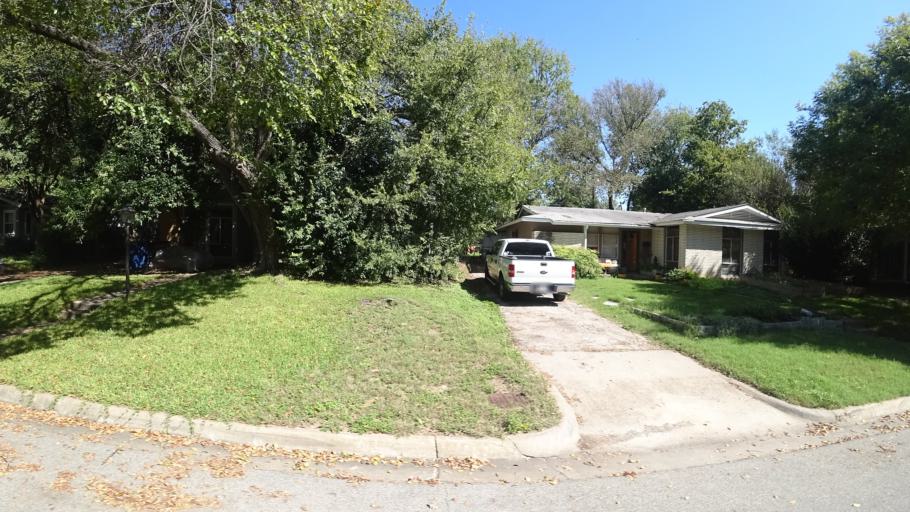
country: US
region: Texas
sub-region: Travis County
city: Austin
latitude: 30.3070
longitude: -97.6987
